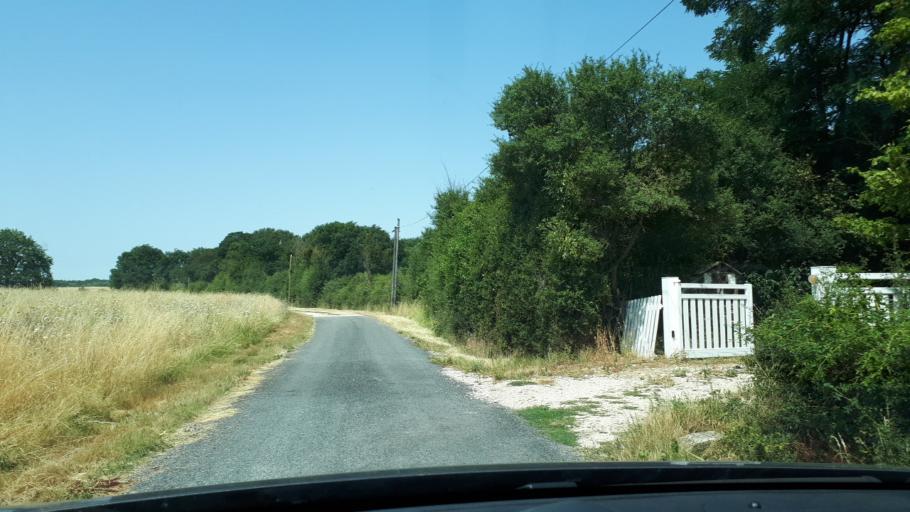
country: FR
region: Centre
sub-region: Departement du Loir-et-Cher
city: Saint-Ouen
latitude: 47.8159
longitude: 1.0657
